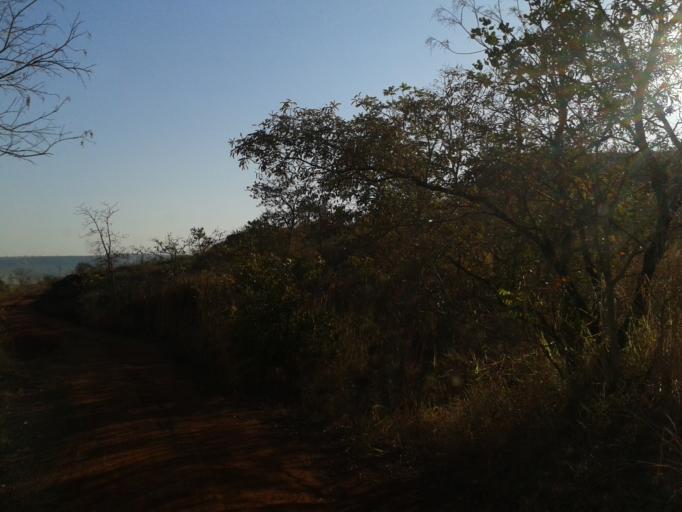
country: BR
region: Minas Gerais
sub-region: Santa Vitoria
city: Santa Vitoria
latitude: -19.1874
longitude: -50.0309
